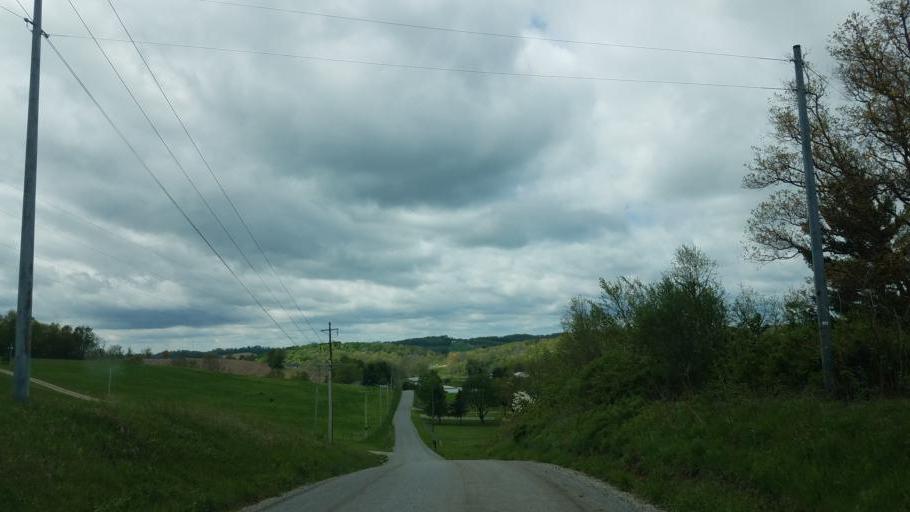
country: US
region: Ohio
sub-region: Ashland County
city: Loudonville
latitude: 40.5548
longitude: -82.3168
